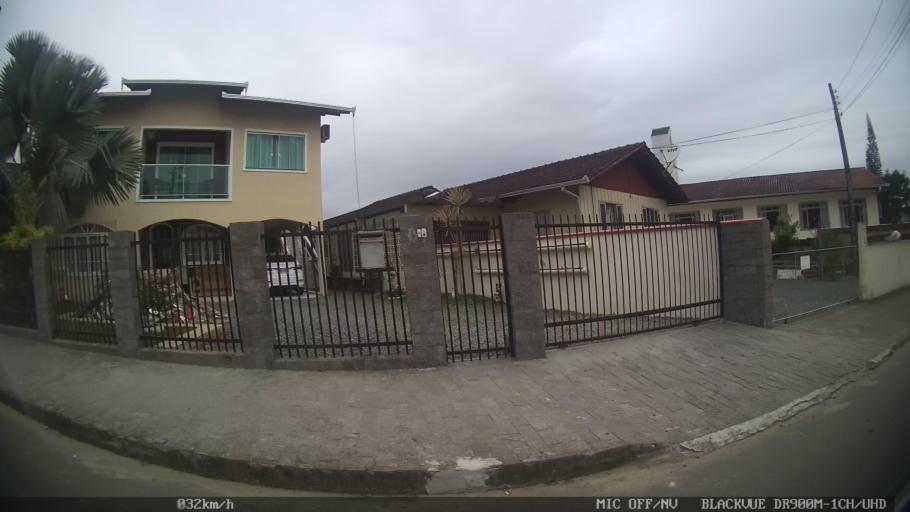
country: BR
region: Santa Catarina
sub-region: Joinville
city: Joinville
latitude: -26.2698
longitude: -48.8265
